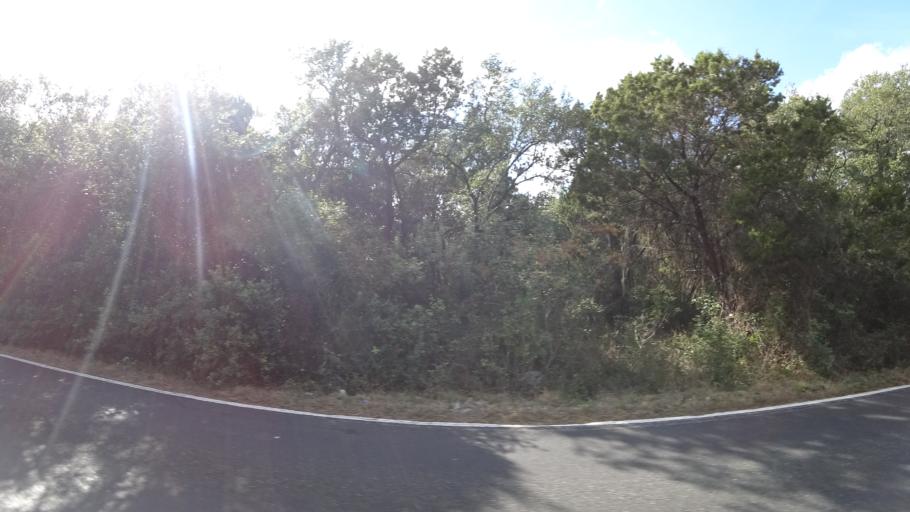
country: US
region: Texas
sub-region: Travis County
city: Barton Creek
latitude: 30.2602
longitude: -97.8884
